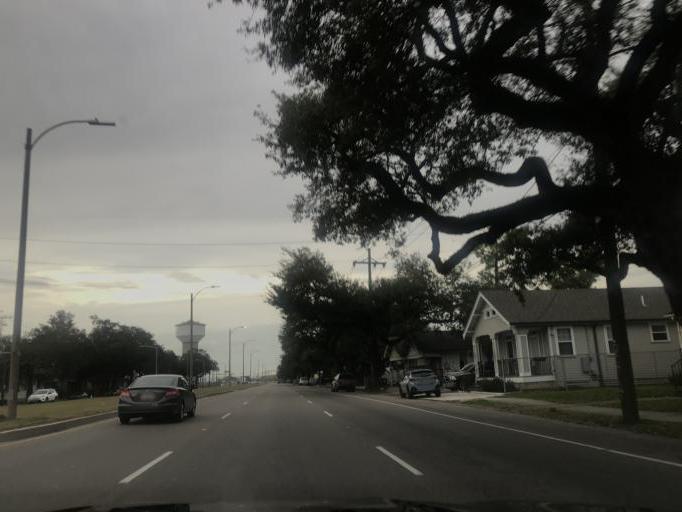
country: US
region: Louisiana
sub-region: Jefferson Parish
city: Jefferson
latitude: 29.9576
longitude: -90.1225
